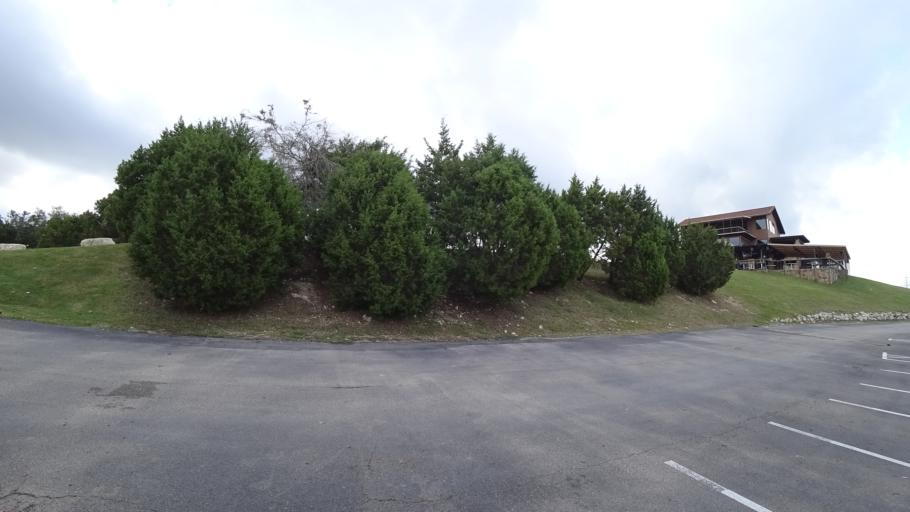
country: US
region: Texas
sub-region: Travis County
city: Hudson Bend
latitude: 30.3908
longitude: -97.8716
